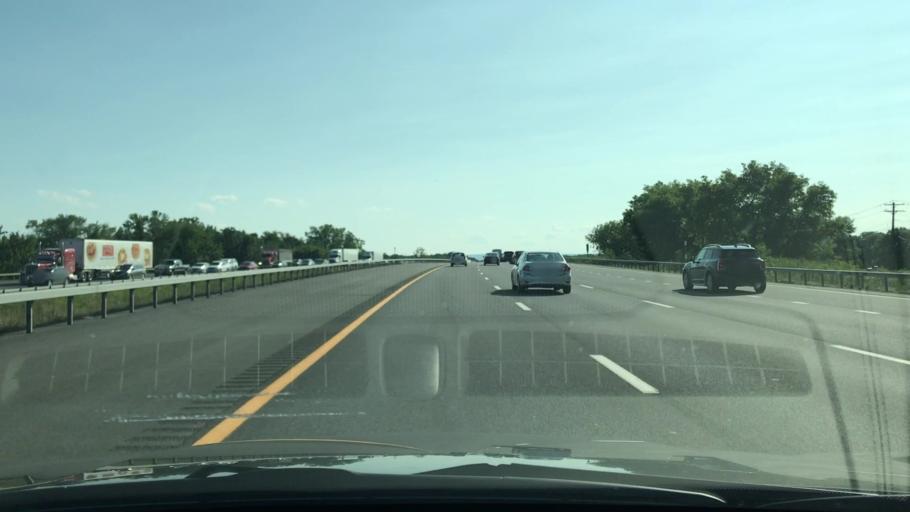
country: US
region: New York
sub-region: Albany County
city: Roessleville
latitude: 42.7295
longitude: -73.7935
